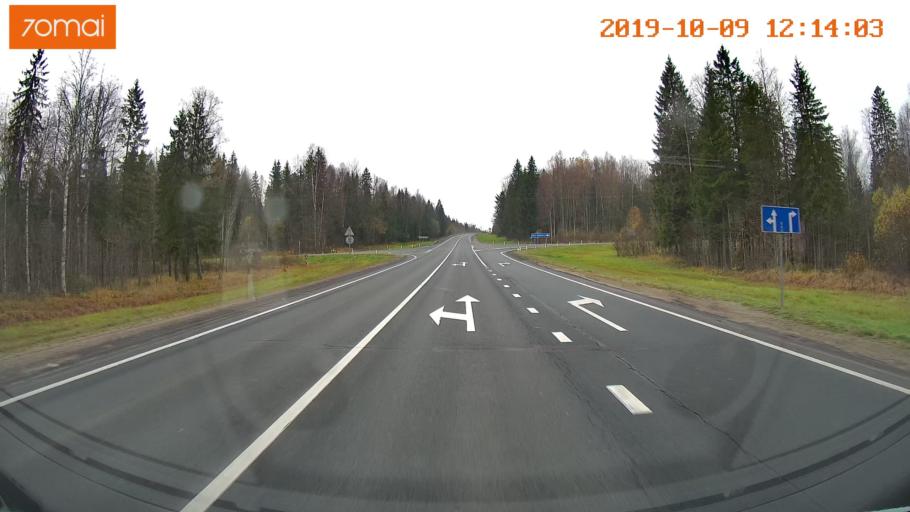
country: RU
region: Jaroslavl
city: Prechistoye
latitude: 58.5013
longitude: 40.3414
